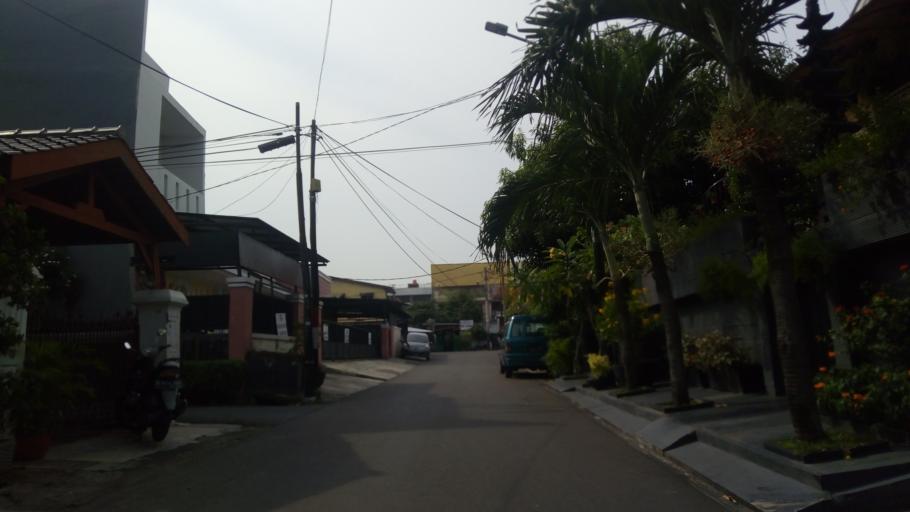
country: ID
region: Jakarta Raya
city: Jakarta
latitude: -6.1706
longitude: 106.8514
